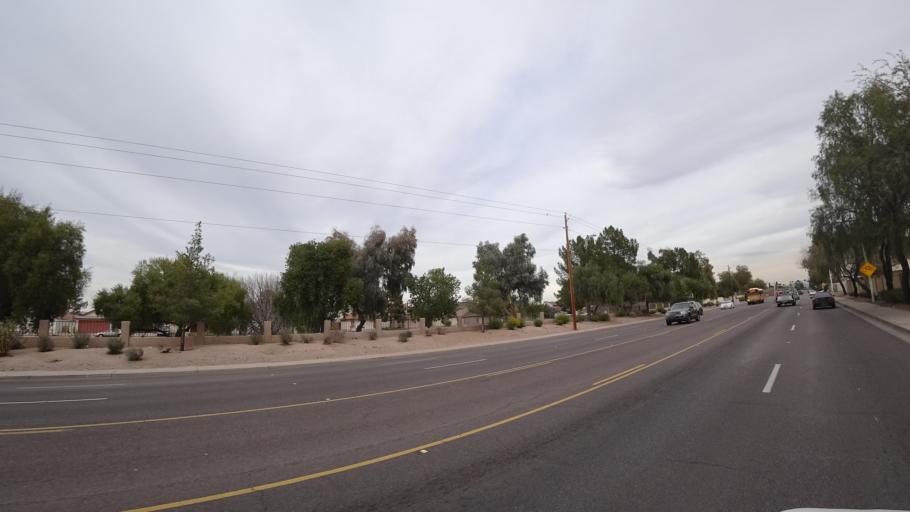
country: US
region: Arizona
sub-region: Maricopa County
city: Peoria
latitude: 33.5817
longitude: -112.1971
